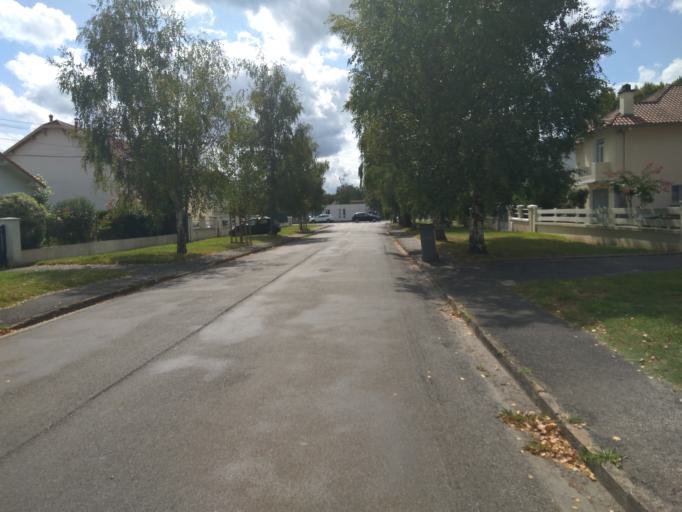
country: FR
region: Aquitaine
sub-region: Departement des Pyrenees-Atlantiques
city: Bizanos
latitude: 43.3064
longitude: -0.3383
